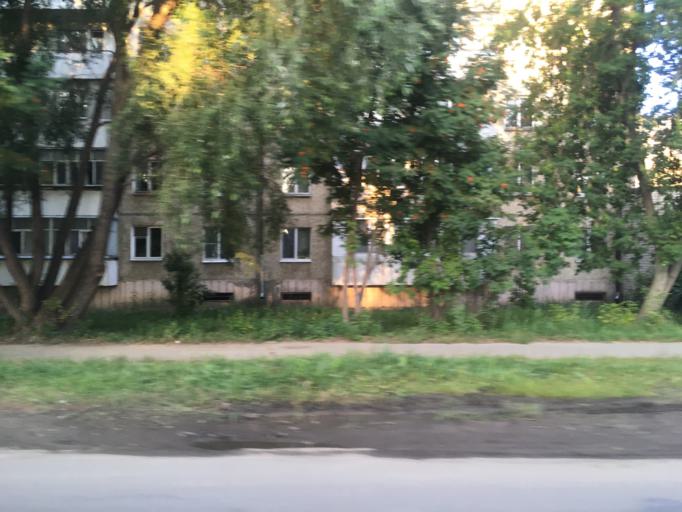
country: RU
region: Mariy-El
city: Yoshkar-Ola
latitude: 56.6479
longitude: 47.8645
